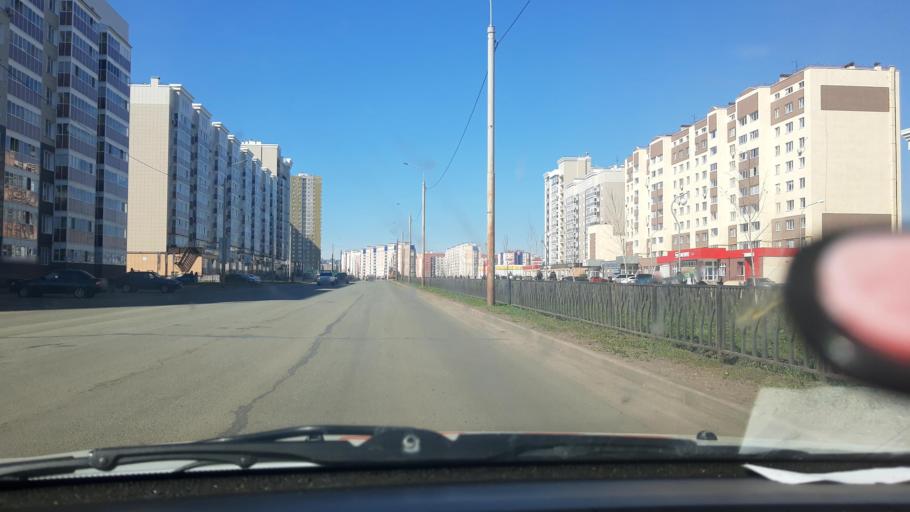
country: RU
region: Bashkortostan
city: Sterlitamak
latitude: 53.6266
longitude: 55.8959
